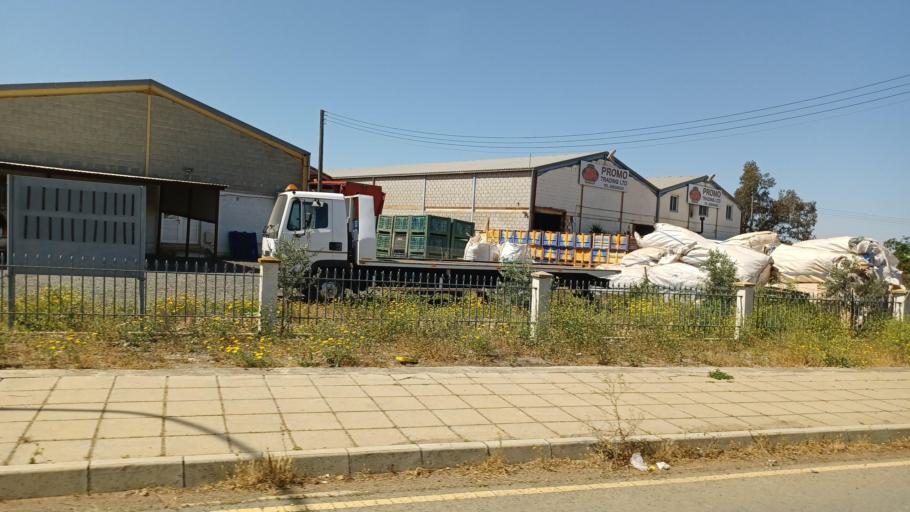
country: CY
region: Lefkosia
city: Kokkinotrimithia
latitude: 35.1531
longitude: 33.2294
